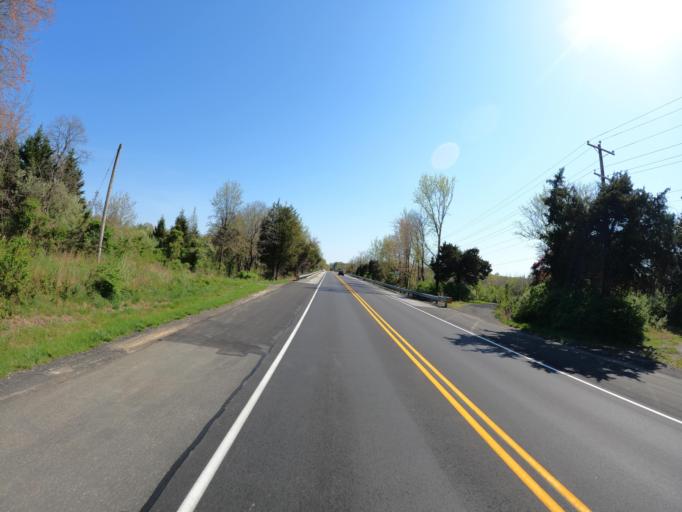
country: US
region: Delaware
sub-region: New Castle County
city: Newark
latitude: 39.6428
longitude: -75.7795
